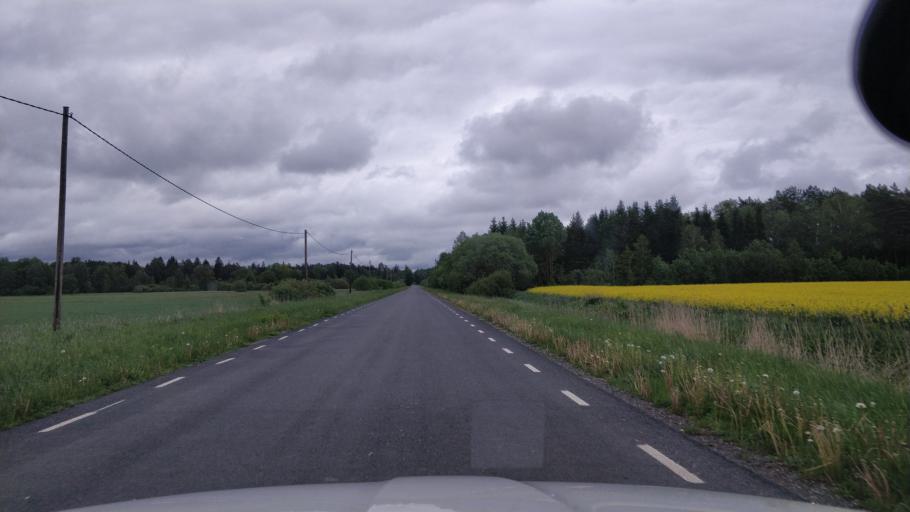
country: EE
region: Raplamaa
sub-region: Maerjamaa vald
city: Marjamaa
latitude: 58.7573
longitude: 24.2424
